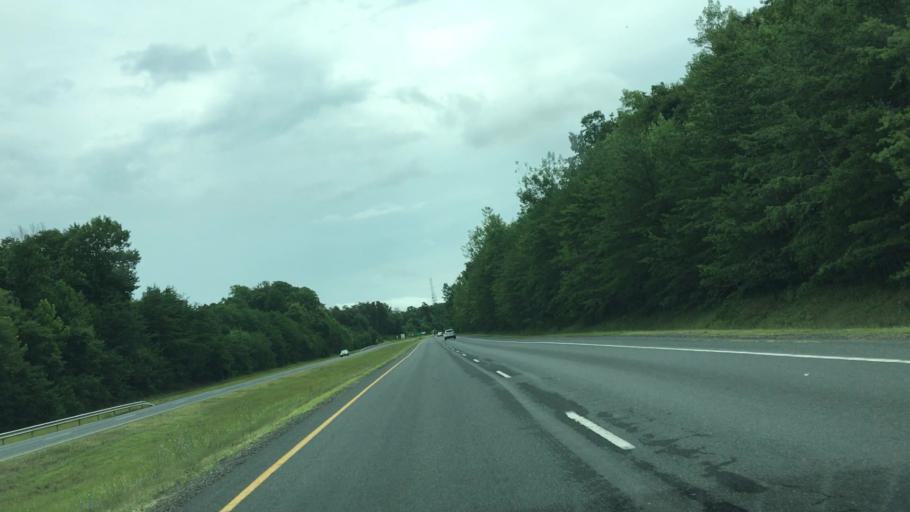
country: US
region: Virginia
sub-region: Prince William County
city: Lake Ridge
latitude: 38.6828
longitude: -77.3683
